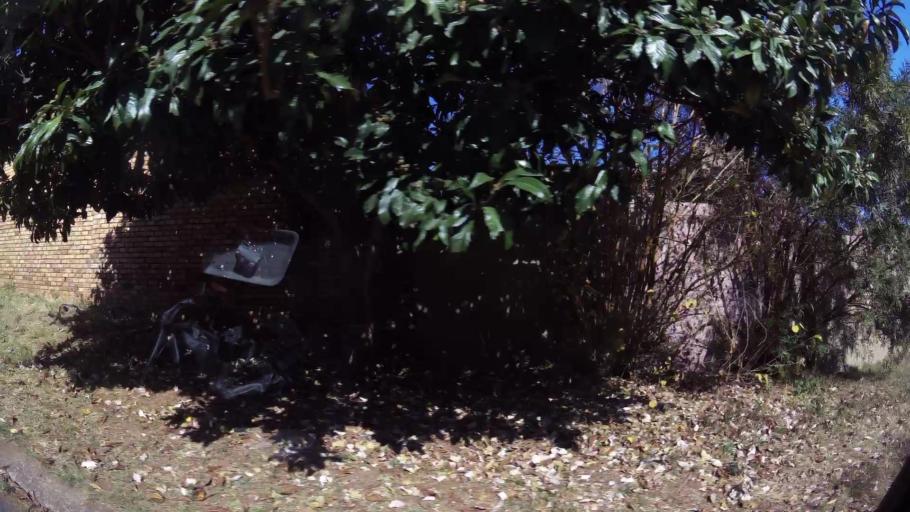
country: ZA
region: Gauteng
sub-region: City of Johannesburg Metropolitan Municipality
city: Johannesburg
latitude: -26.2632
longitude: 28.0503
